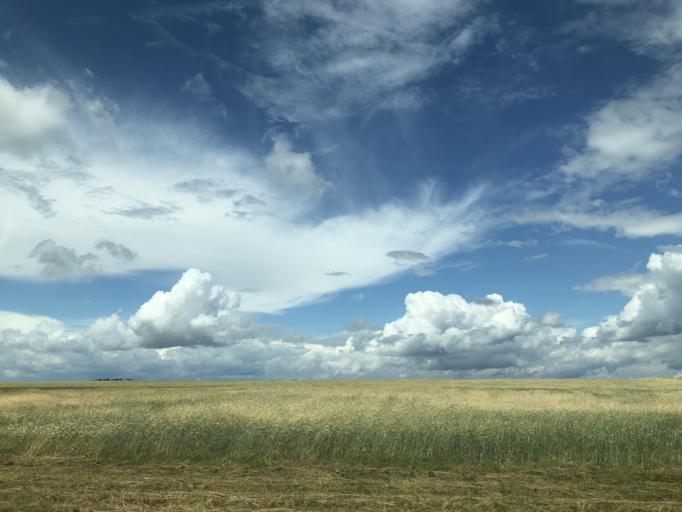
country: BY
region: Minsk
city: Tsimkavichy
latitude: 53.2495
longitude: 26.8988
